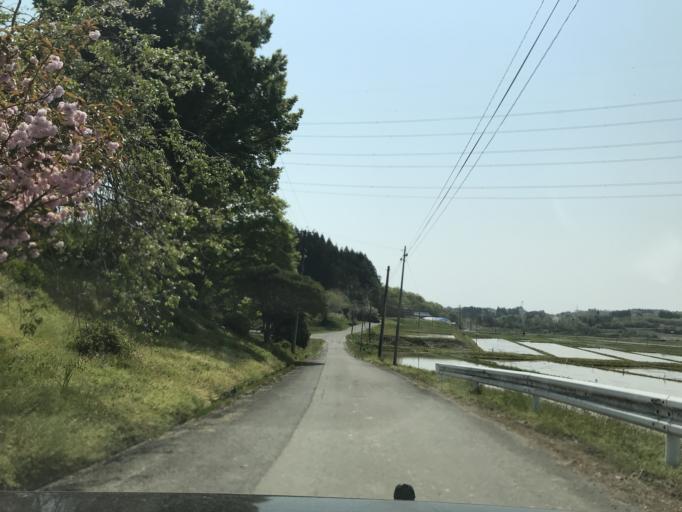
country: JP
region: Iwate
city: Ichinoseki
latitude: 38.8565
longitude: 141.0850
